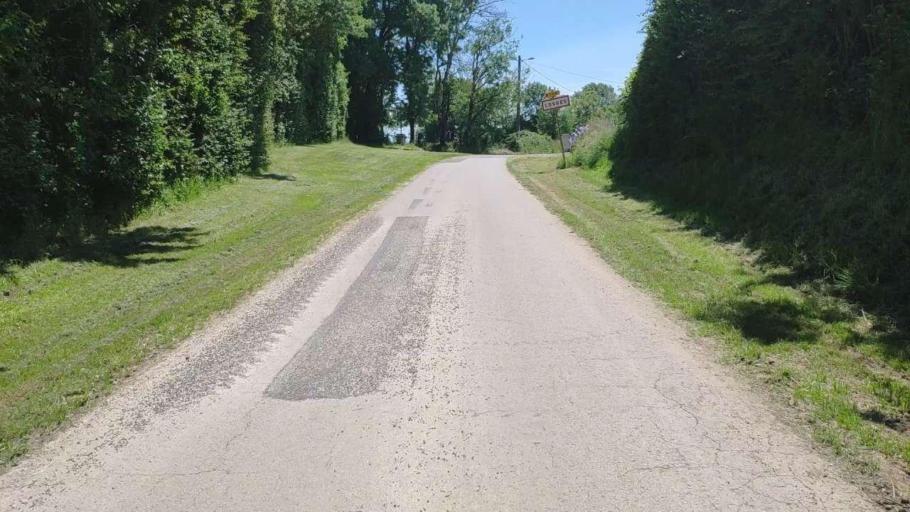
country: FR
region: Franche-Comte
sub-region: Departement du Jura
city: Bletterans
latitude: 46.7519
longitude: 5.4031
